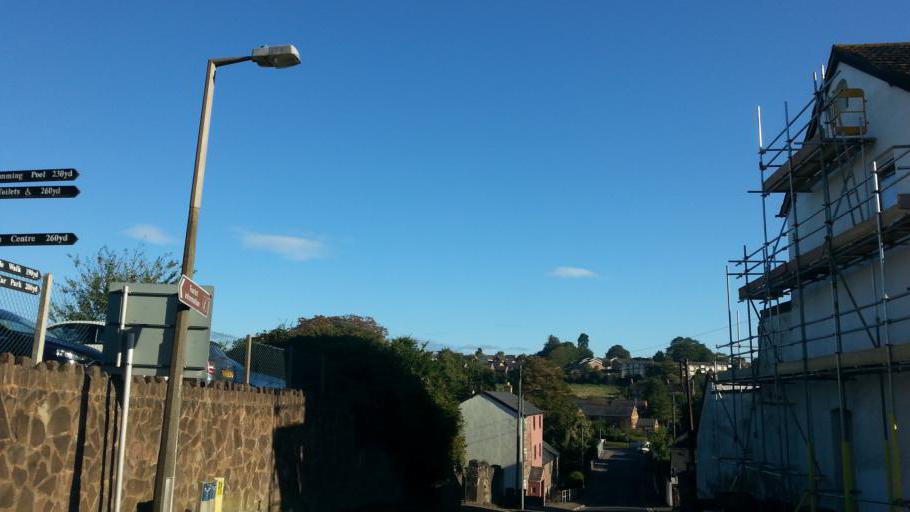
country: GB
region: England
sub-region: Herefordshire
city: Ross on Wye
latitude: 51.9165
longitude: -2.5855
